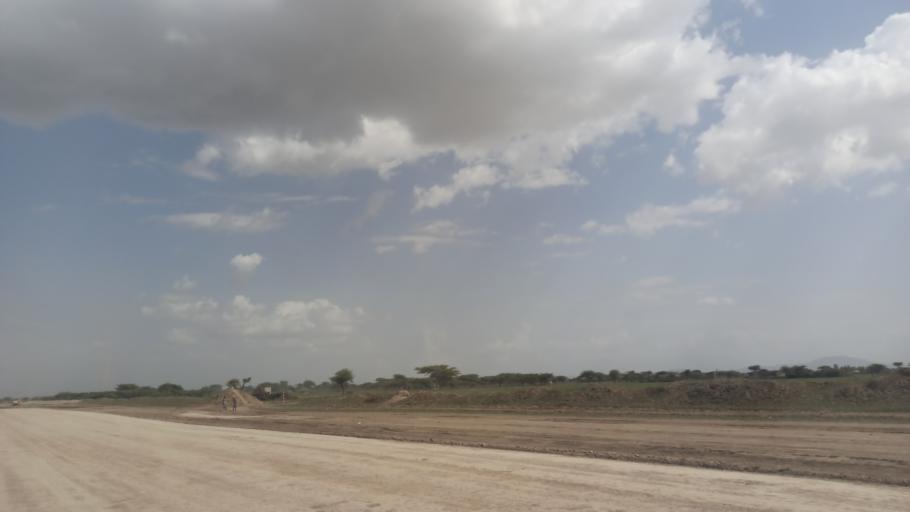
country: ET
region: Oromiya
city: Ziway
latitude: 7.7387
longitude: 38.6210
